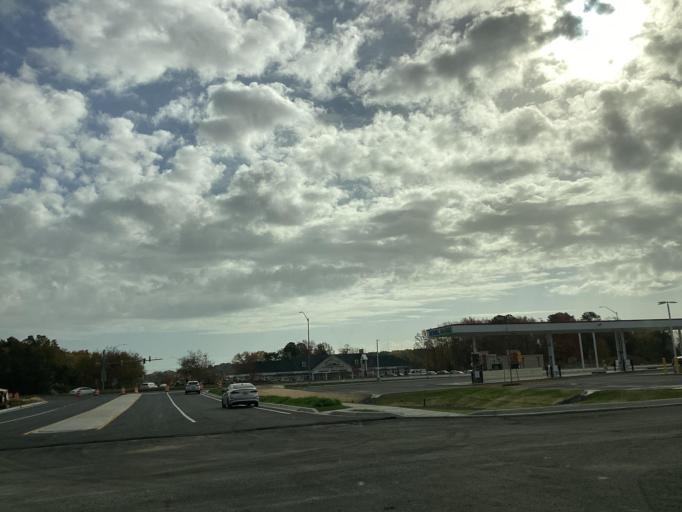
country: US
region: Maryland
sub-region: Somerset County
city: Princess Anne
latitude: 38.2200
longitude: -75.6994
